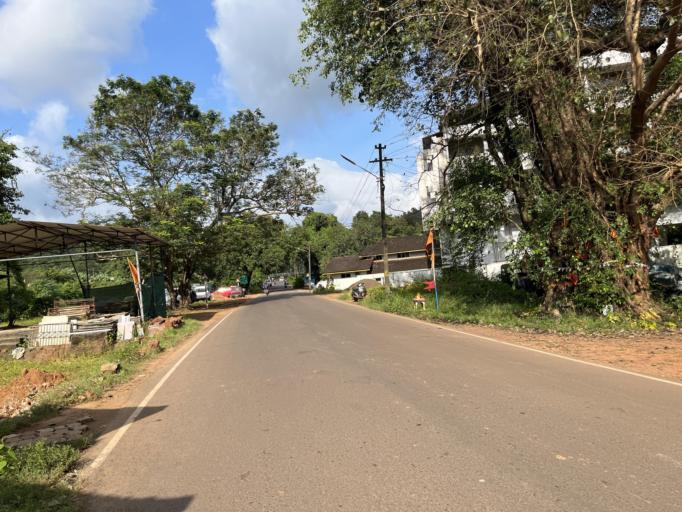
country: IN
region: Goa
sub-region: North Goa
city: Ponda
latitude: 15.4081
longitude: 74.0206
